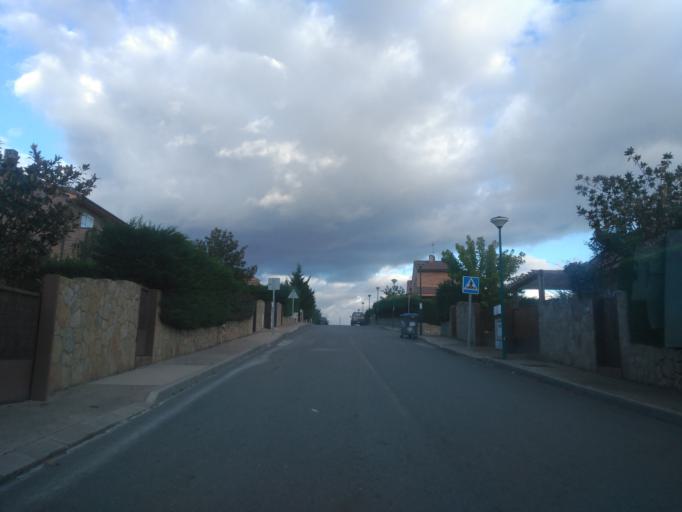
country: ES
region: Castille and Leon
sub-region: Provincia de Salamanca
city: Villamayor
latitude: 40.9826
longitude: -5.7055
